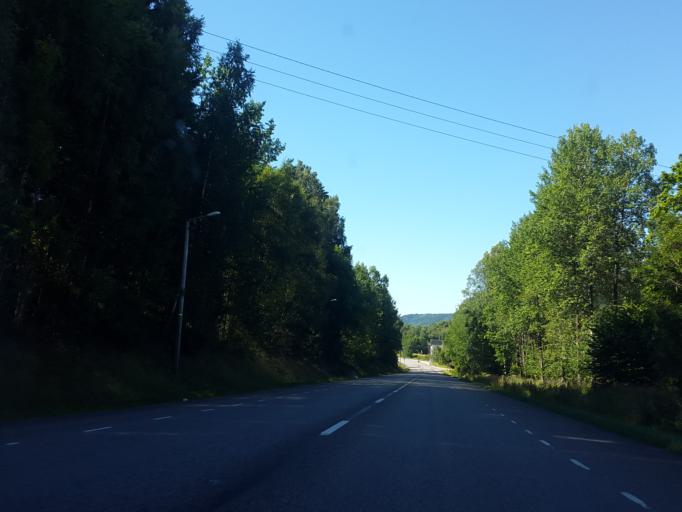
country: SE
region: Vaestra Goetaland
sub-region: Boras Kommun
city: Boras
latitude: 57.7790
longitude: 12.9860
